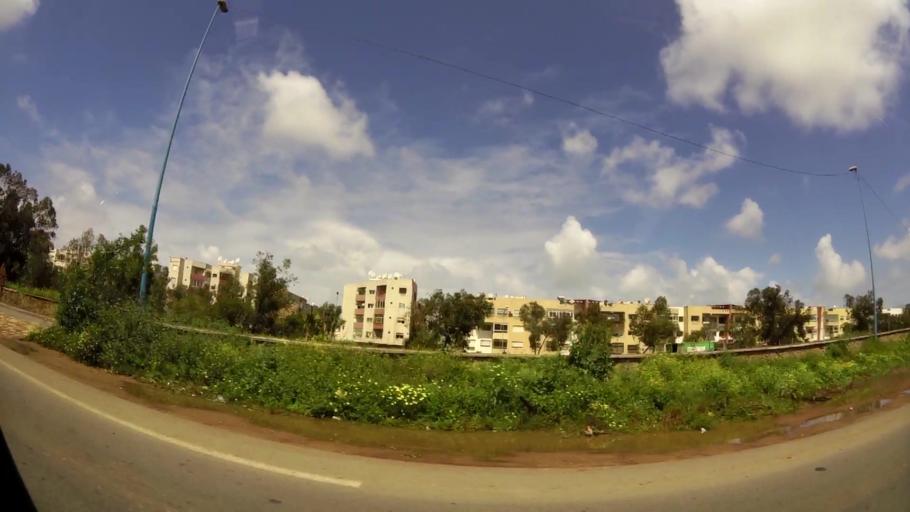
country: MA
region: Grand Casablanca
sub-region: Mediouna
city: Tit Mellil
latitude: 33.6133
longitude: -7.4847
